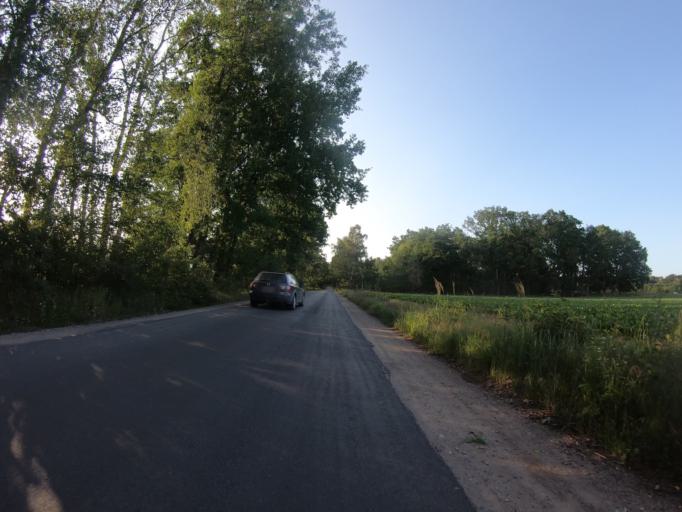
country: DE
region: Lower Saxony
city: Wagenhoff
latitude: 52.5163
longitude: 10.4803
